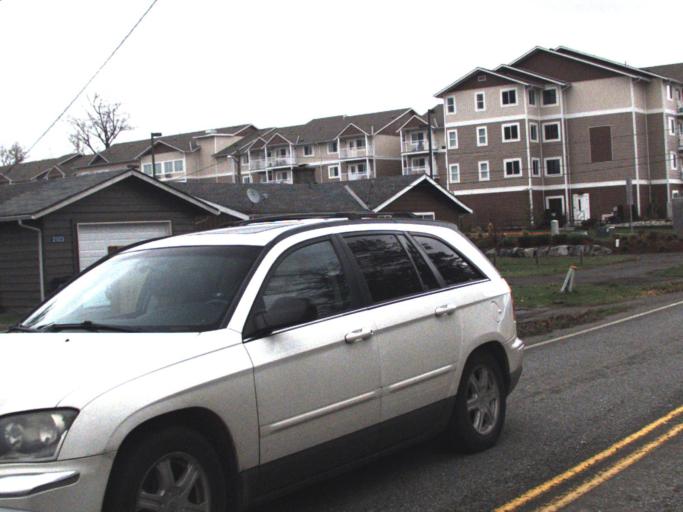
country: US
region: Washington
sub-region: Snohomish County
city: Smokey Point
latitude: 48.1520
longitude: -122.2017
